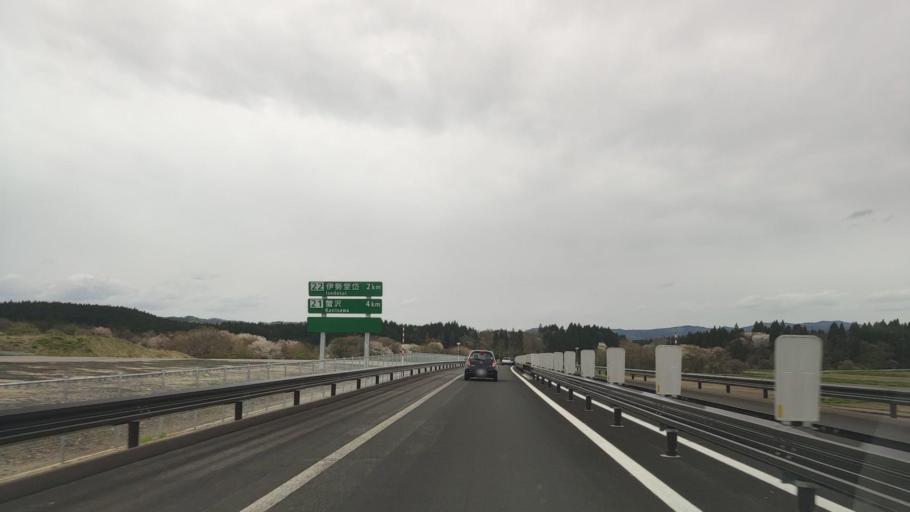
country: JP
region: Akita
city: Takanosu
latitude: 40.2002
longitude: 140.3583
